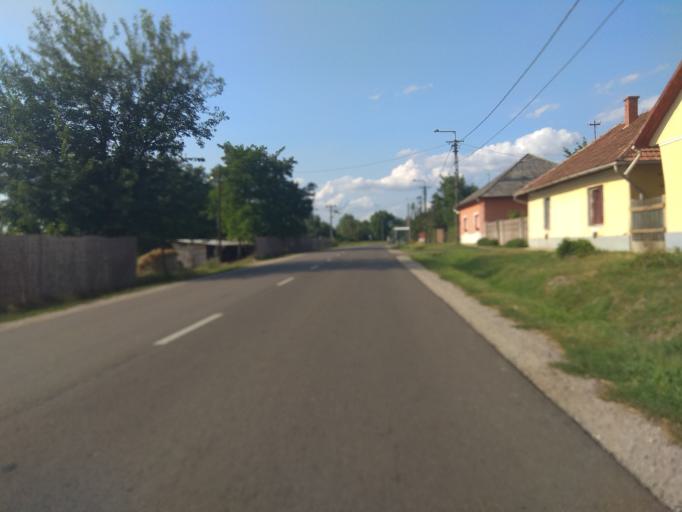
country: HU
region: Borsod-Abauj-Zemplen
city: Mezocsat
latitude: 47.8309
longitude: 20.9011
